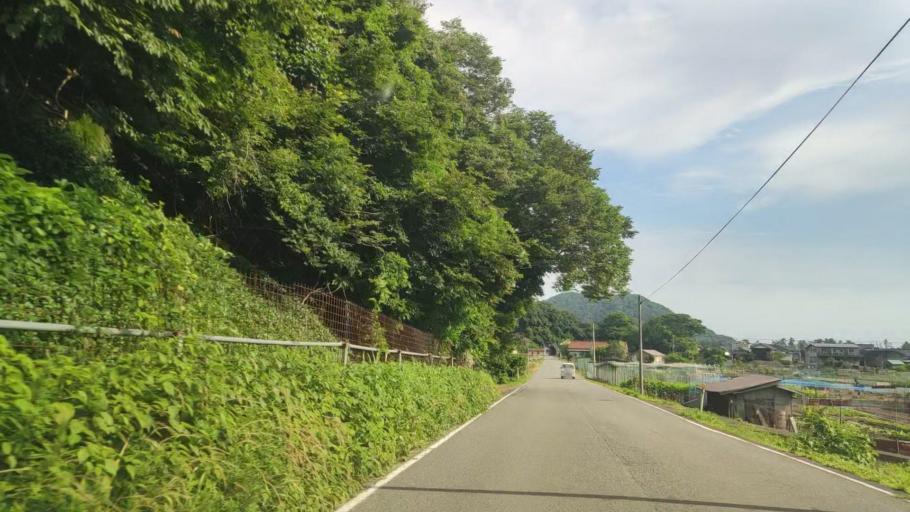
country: JP
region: Hyogo
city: Toyooka
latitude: 35.6360
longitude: 134.8366
